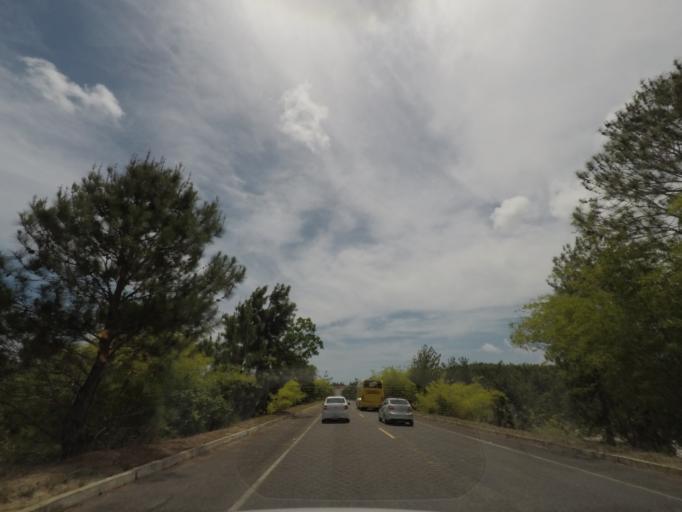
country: BR
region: Bahia
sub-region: Conde
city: Conde
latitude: -11.9862
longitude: -37.6776
